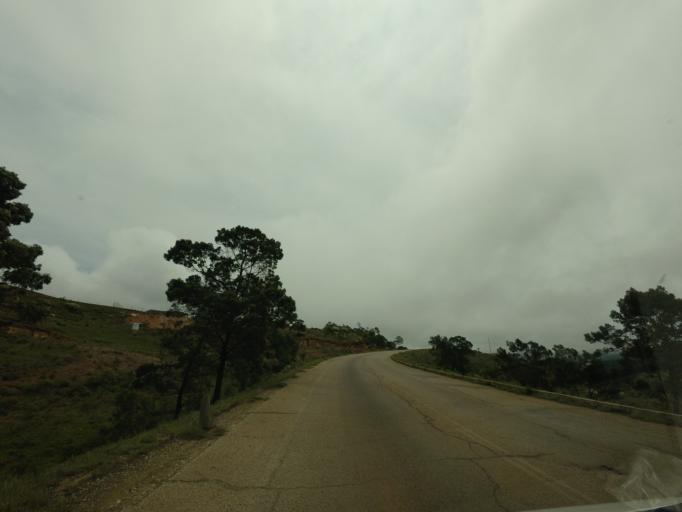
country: SZ
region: Hhohho
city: Piggs Peak
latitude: -26.0128
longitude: 31.2583
